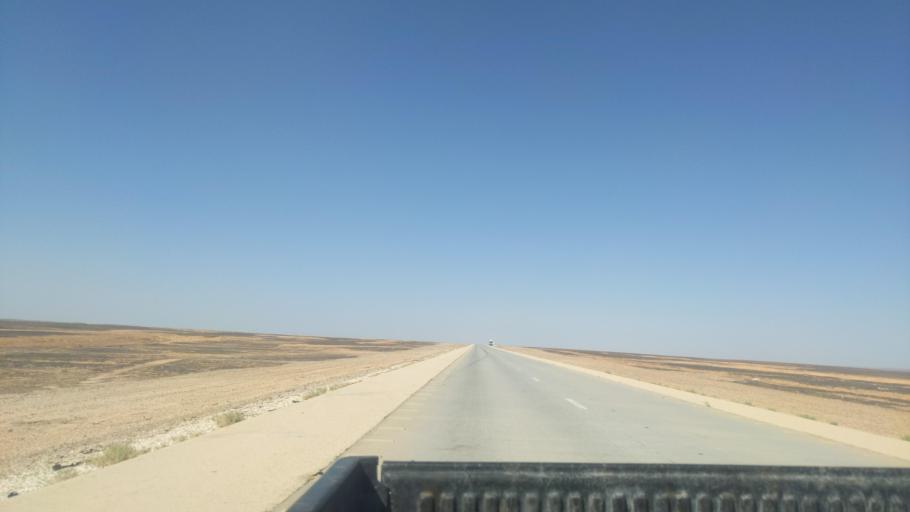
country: JO
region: Amman
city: Al Azraq ash Shamali
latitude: 31.4316
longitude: 36.7385
